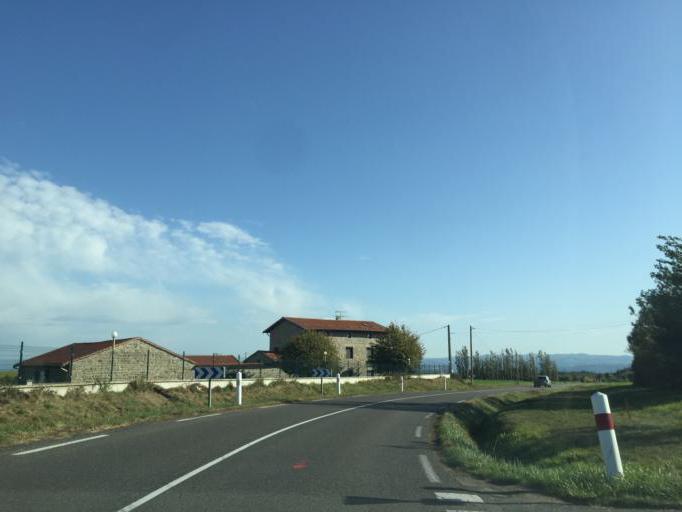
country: FR
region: Rhone-Alpes
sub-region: Departement de la Loire
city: Perigneux
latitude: 45.4694
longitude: 4.1322
